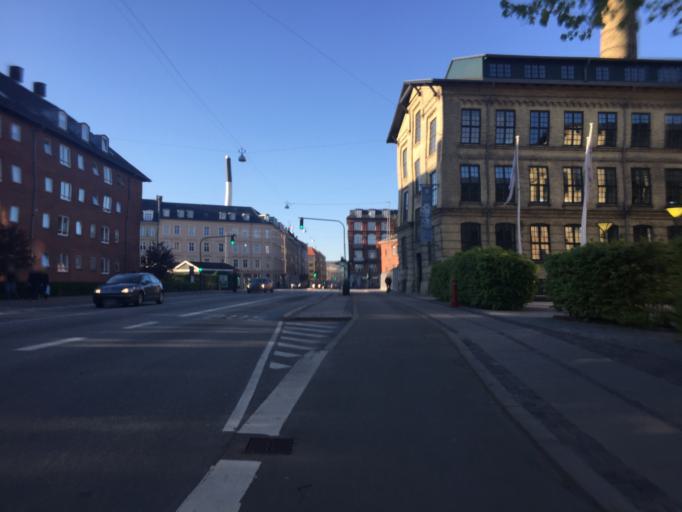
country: DK
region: Capital Region
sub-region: Frederiksberg Kommune
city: Frederiksberg
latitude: 55.6783
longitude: 12.5211
